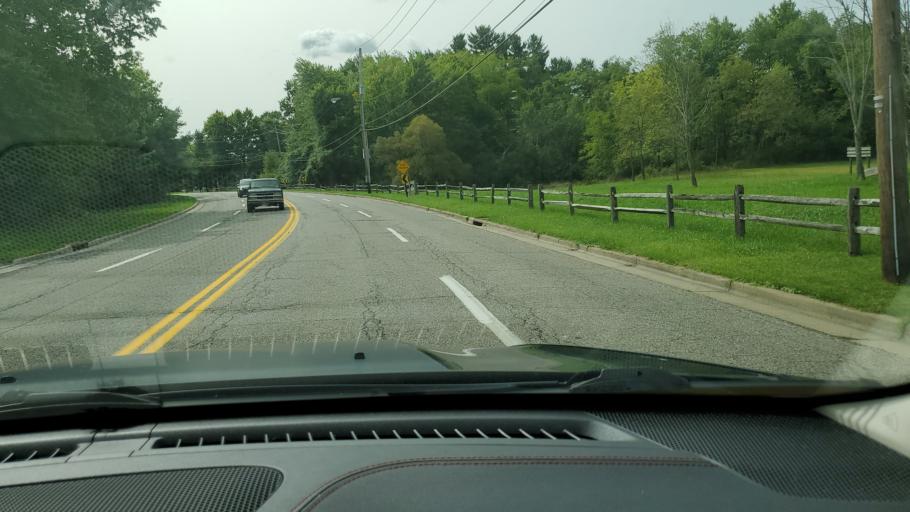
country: US
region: Ohio
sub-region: Mahoning County
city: Boardman
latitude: 40.9936
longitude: -80.6723
